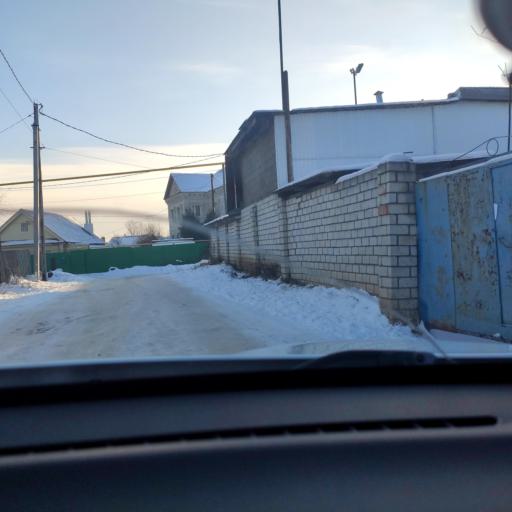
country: RU
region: Tatarstan
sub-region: Gorod Kazan'
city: Kazan
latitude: 55.7293
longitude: 49.1383
